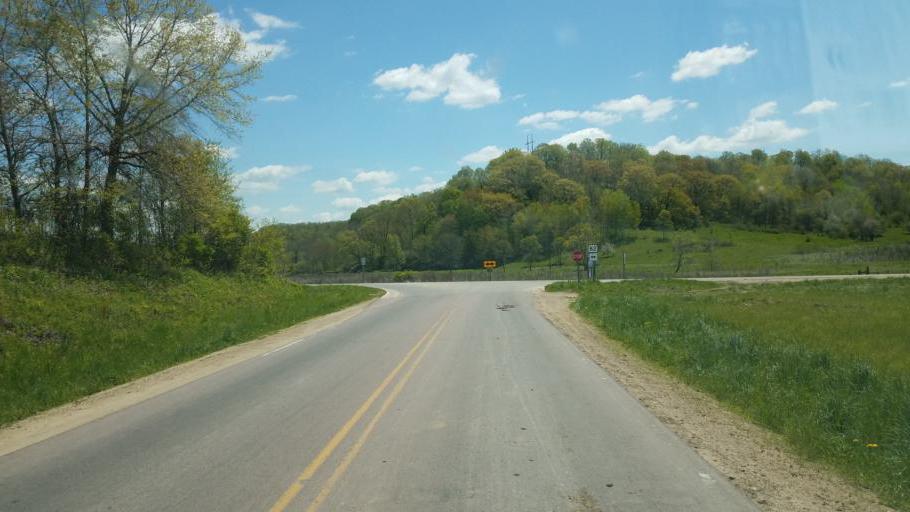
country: US
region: Wisconsin
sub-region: Vernon County
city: Hillsboro
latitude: 43.6449
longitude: -90.4372
